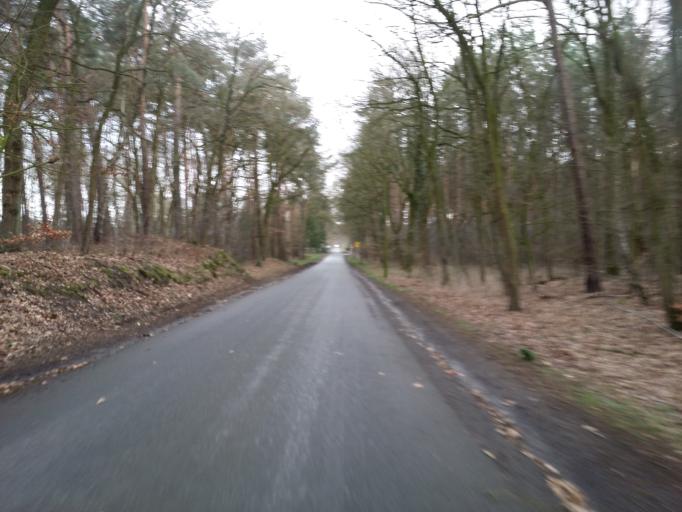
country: DE
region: Lower Saxony
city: Gross Ippener
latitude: 52.9735
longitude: 8.6296
